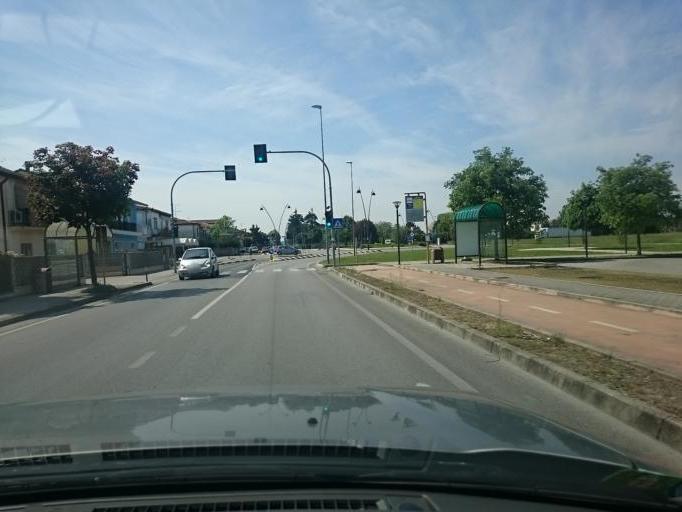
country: IT
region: Veneto
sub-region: Provincia di Padova
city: Cartura
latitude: 45.2826
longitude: 11.8697
